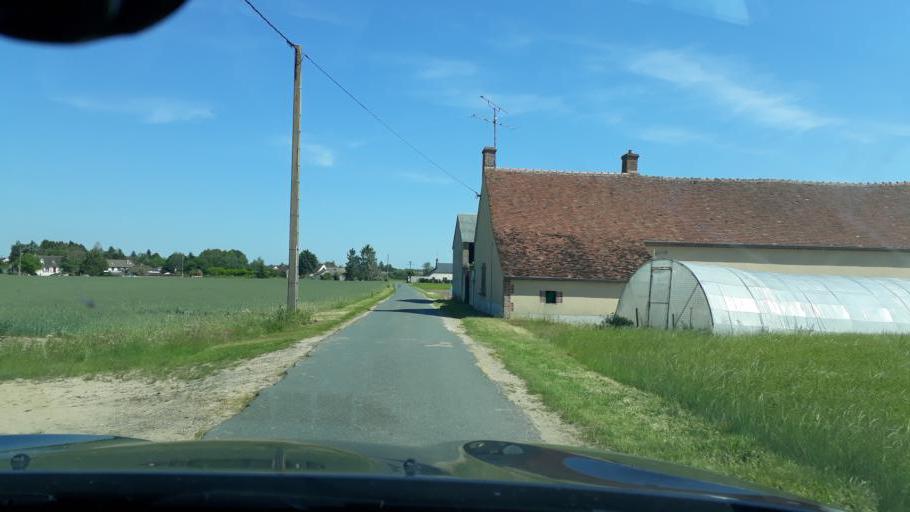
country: FR
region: Centre
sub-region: Departement du Loiret
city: Saint-Benoit-sur-Loire
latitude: 47.8067
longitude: 2.2628
